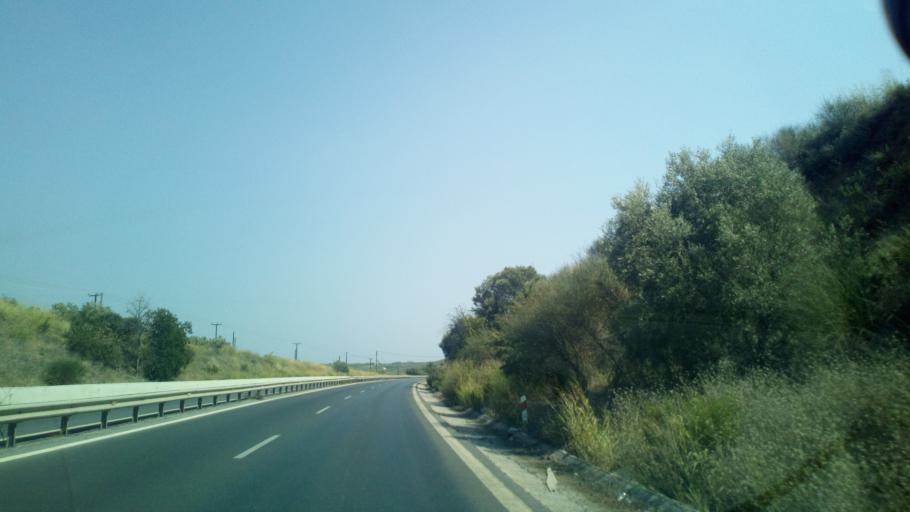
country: GR
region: Central Macedonia
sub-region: Nomos Chalkidikis
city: Nea Moudhania
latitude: 40.2592
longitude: 23.2828
